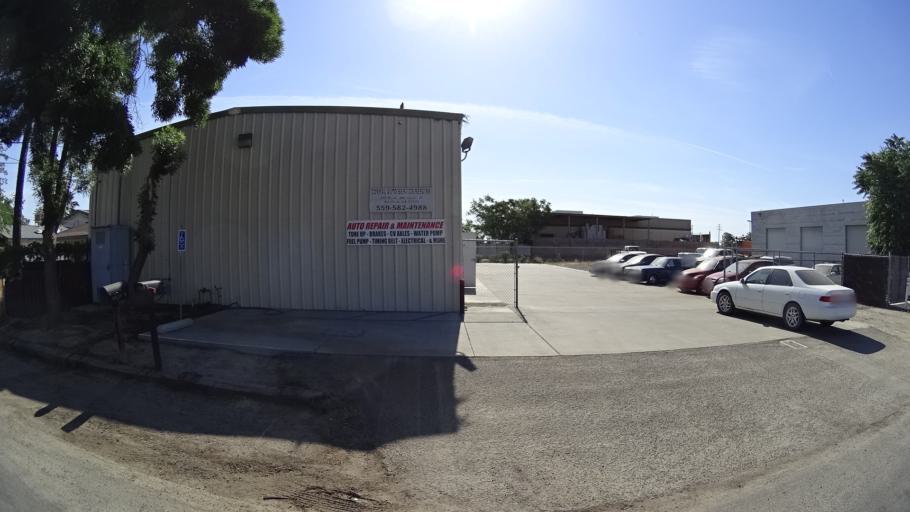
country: US
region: California
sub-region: Kings County
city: Hanford
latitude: 36.3291
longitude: -119.6346
